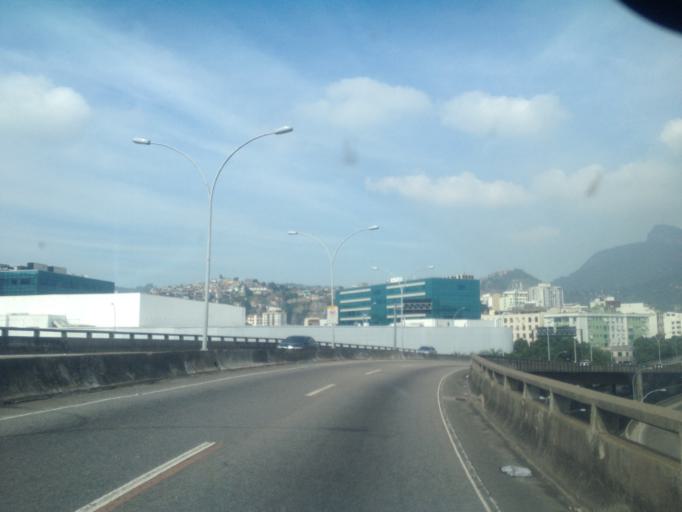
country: BR
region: Rio de Janeiro
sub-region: Rio De Janeiro
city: Rio de Janeiro
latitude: -22.9107
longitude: -43.2098
